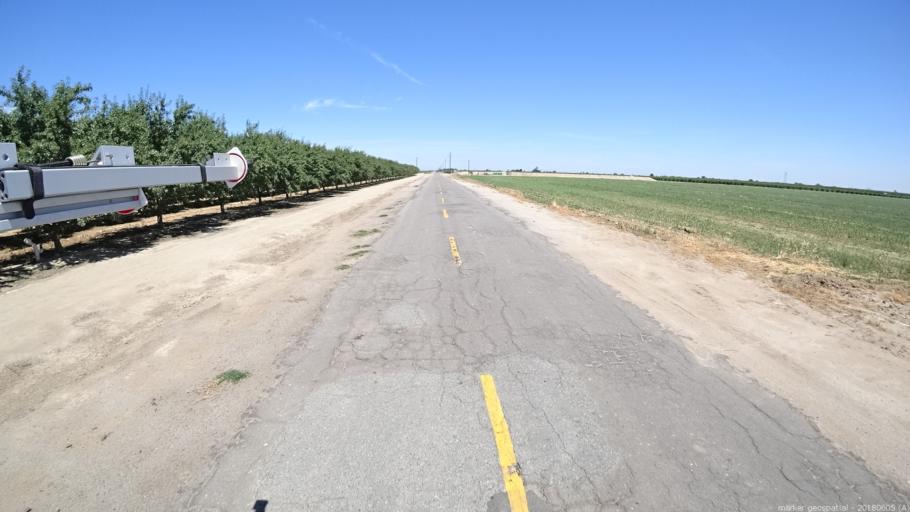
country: US
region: California
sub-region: Madera County
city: Chowchilla
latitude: 37.0906
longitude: -120.3764
